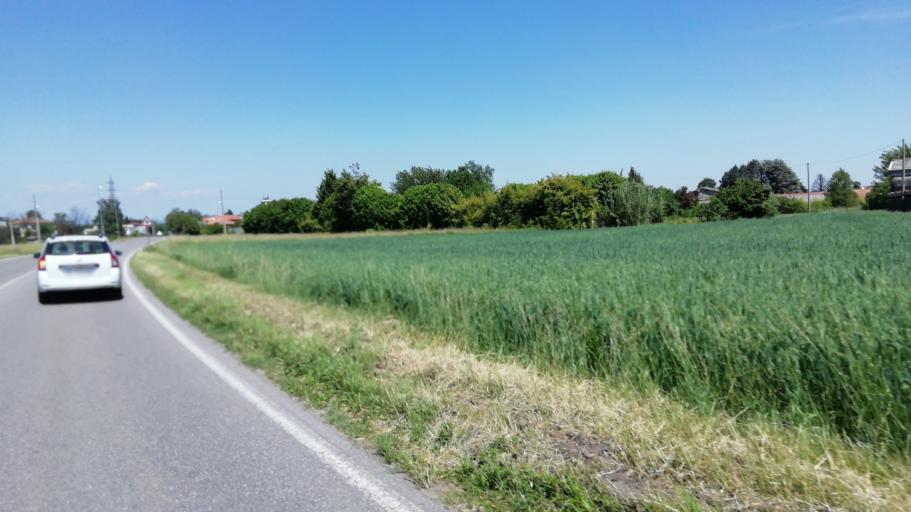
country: IT
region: Lombardy
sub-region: Provincia di Varese
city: Lonate Pozzolo
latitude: 45.6016
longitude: 8.7442
